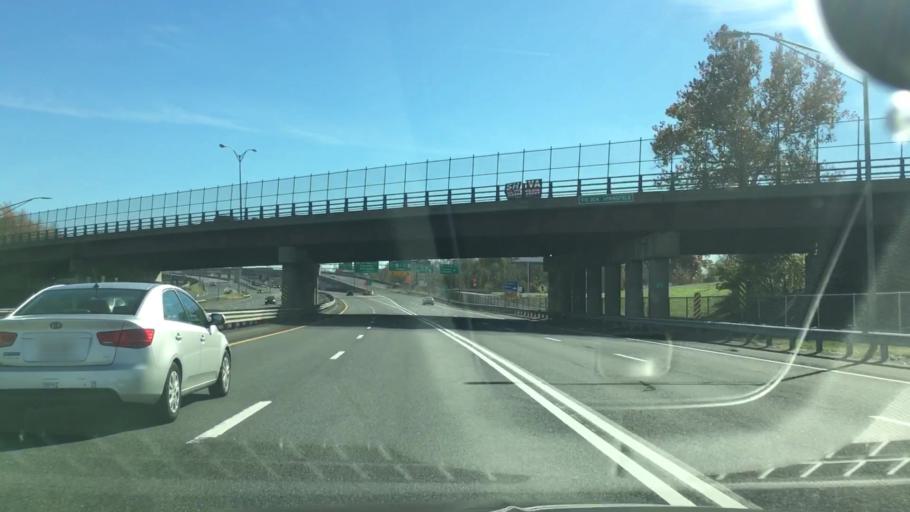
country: US
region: Massachusetts
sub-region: Hampden County
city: West Springfield
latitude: 42.1119
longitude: -72.6069
